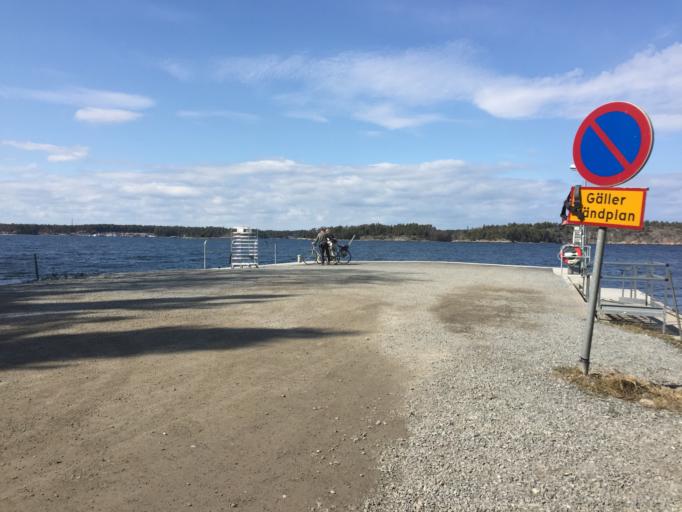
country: SE
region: Stockholm
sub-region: Varmdo Kommun
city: Holo
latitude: 59.2800
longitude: 18.7317
